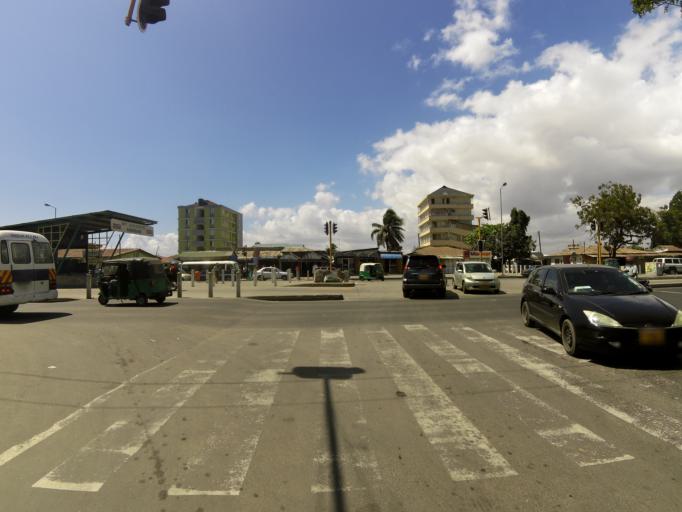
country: TZ
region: Dar es Salaam
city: Magomeni
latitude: -6.8040
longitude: 39.2600
